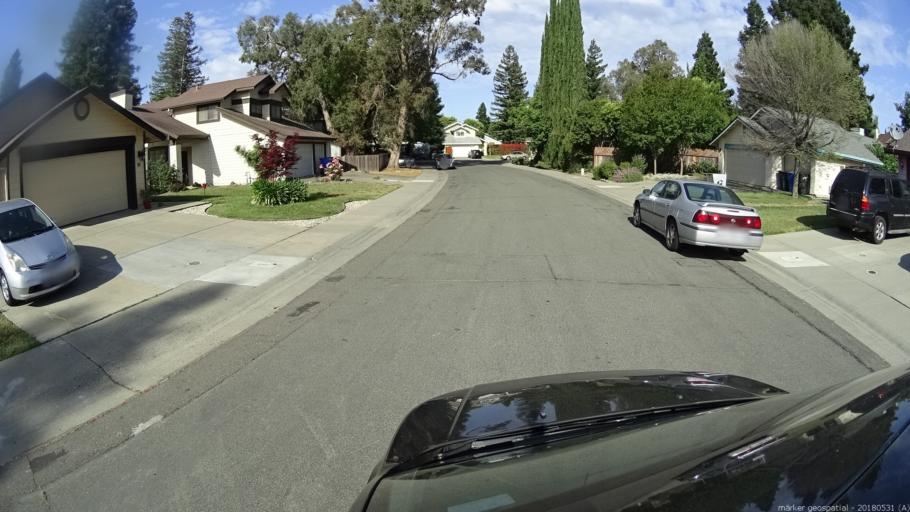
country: US
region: California
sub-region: Sacramento County
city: Sacramento
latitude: 38.6310
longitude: -121.4862
